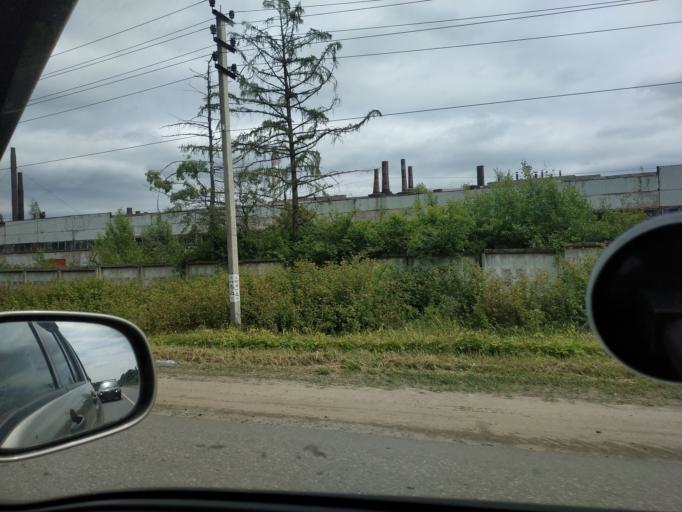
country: RU
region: Moskovskaya
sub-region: Shchelkovskiy Rayon
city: Grebnevo
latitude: 55.9689
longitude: 38.0851
